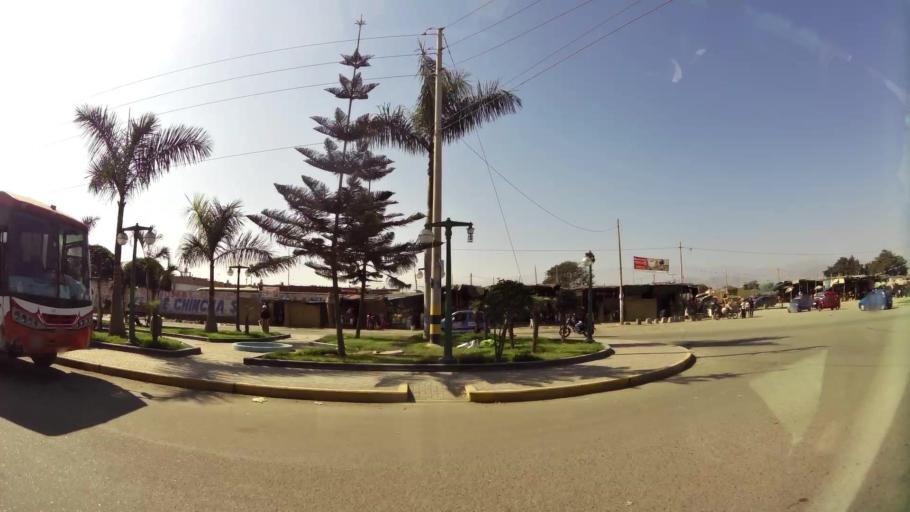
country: PE
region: Ica
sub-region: Provincia de Chincha
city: Chincha Alta
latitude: -13.4110
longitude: -76.1261
